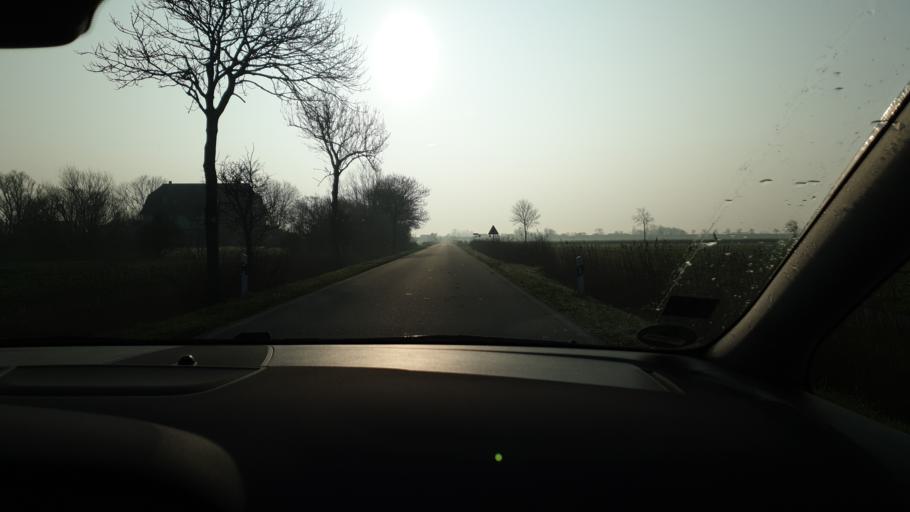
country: DE
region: Schleswig-Holstein
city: Elisabeth-Sophien-Koog
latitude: 54.4978
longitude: 8.9019
